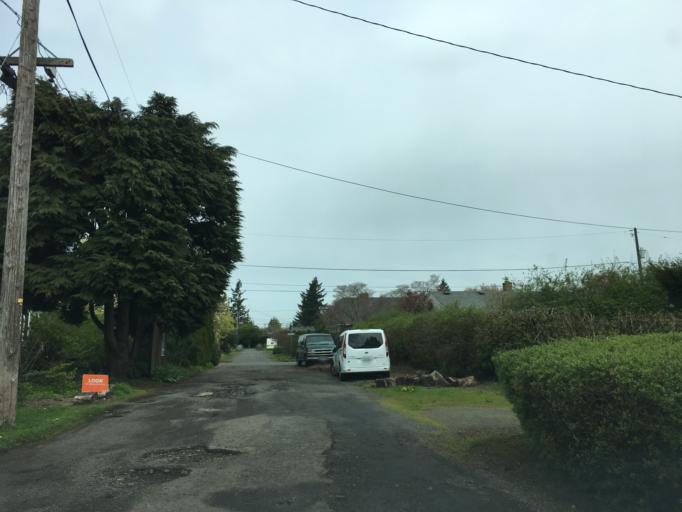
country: US
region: Oregon
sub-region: Multnomah County
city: Lents
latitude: 45.5429
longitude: -122.5853
